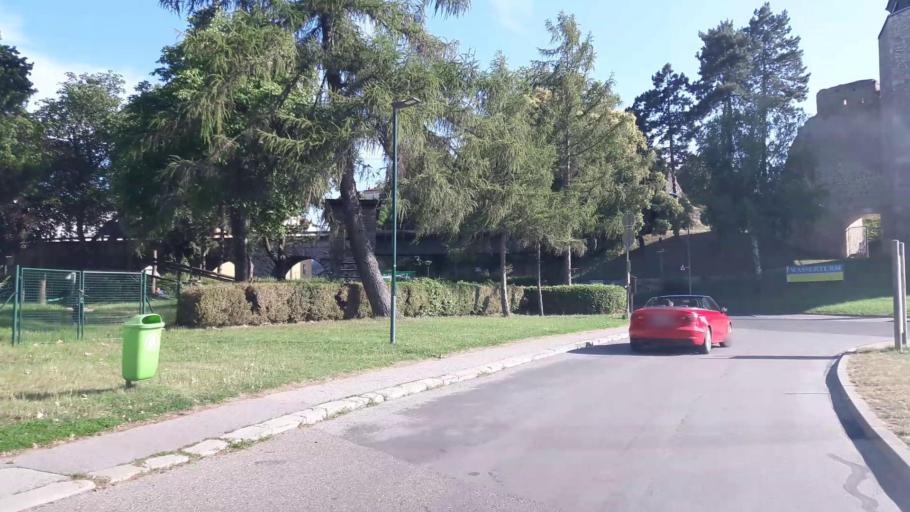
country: AT
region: Lower Austria
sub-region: Politischer Bezirk Bruck an der Leitha
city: Hainburg an der Donau
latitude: 48.1506
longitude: 16.9443
